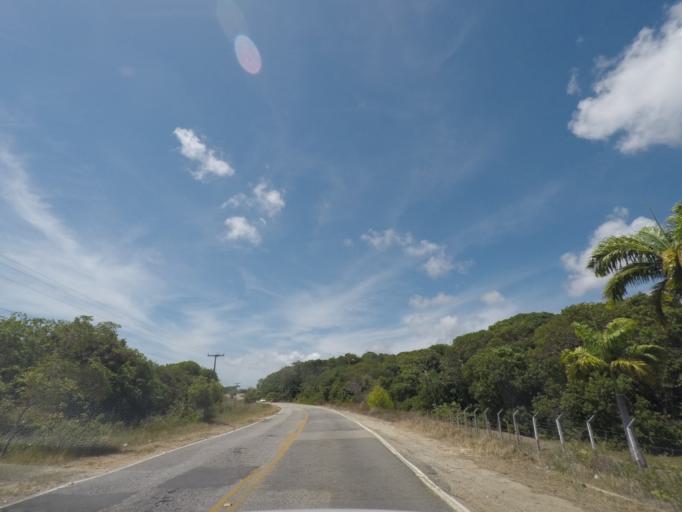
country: BR
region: Sergipe
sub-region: Sao Cristovao
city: Sao Cristovao
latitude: -11.1201
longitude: -37.1842
